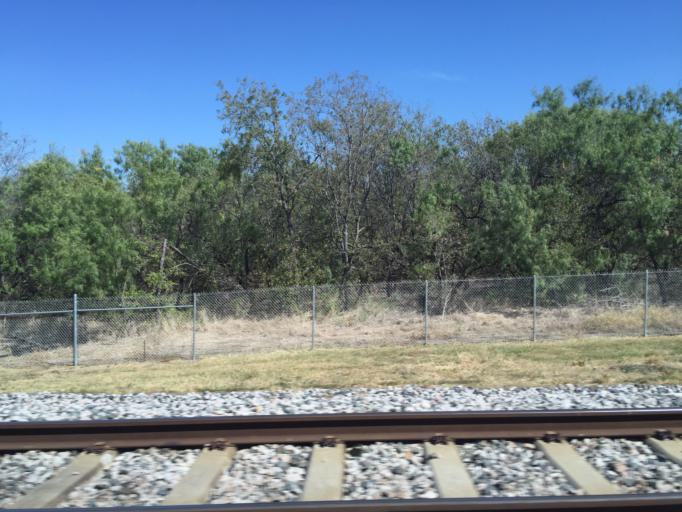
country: US
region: Texas
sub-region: Dallas County
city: Irving
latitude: 32.8761
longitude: -96.9770
